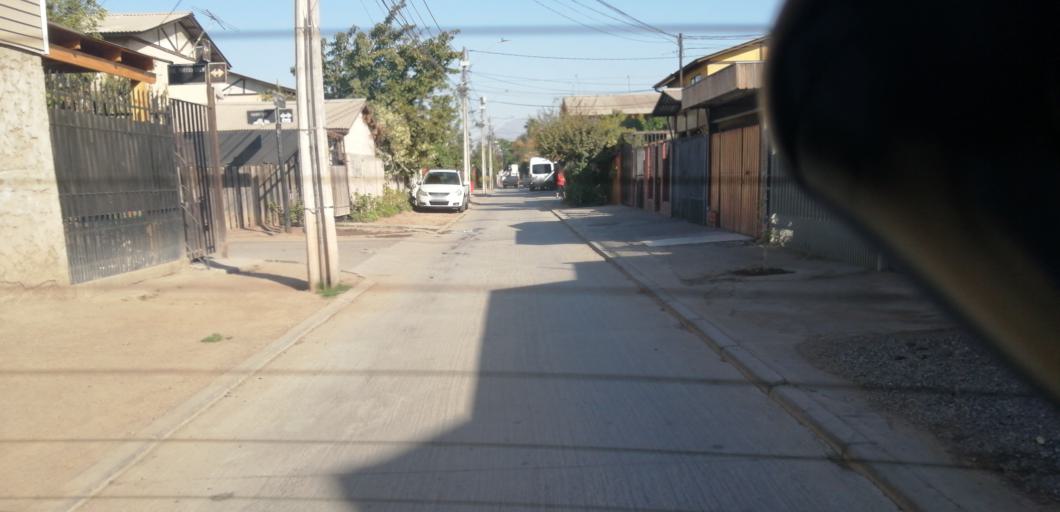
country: CL
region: Santiago Metropolitan
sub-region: Provincia de Santiago
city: Lo Prado
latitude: -33.4592
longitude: -70.7433
